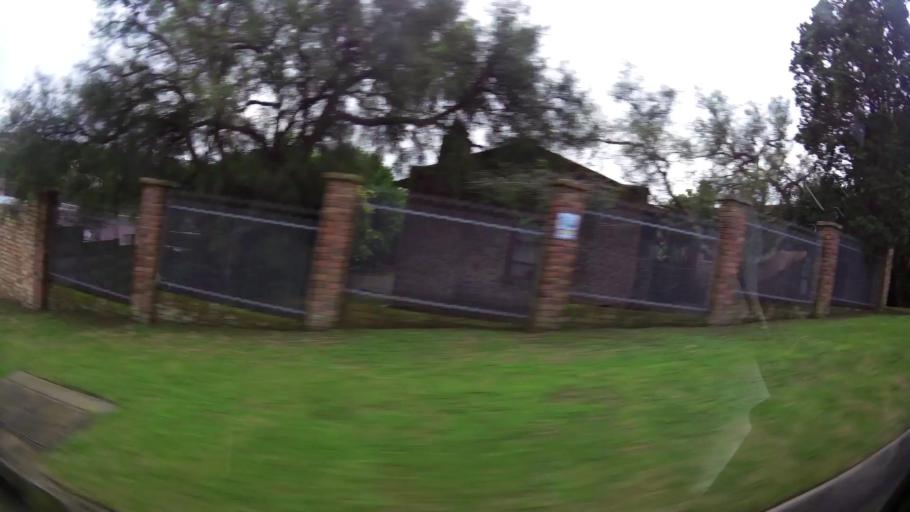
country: ZA
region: Eastern Cape
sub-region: Nelson Mandela Bay Metropolitan Municipality
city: Port Elizabeth
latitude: -34.0010
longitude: 25.5304
